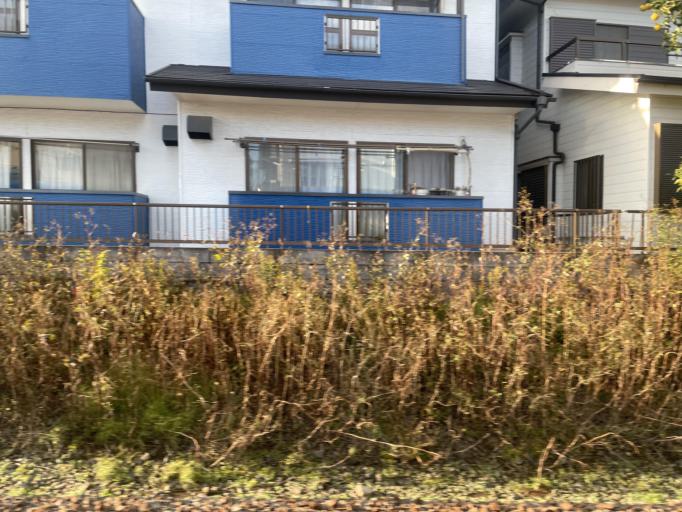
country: JP
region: Saitama
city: Iwatsuki
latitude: 35.9461
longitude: 139.6878
